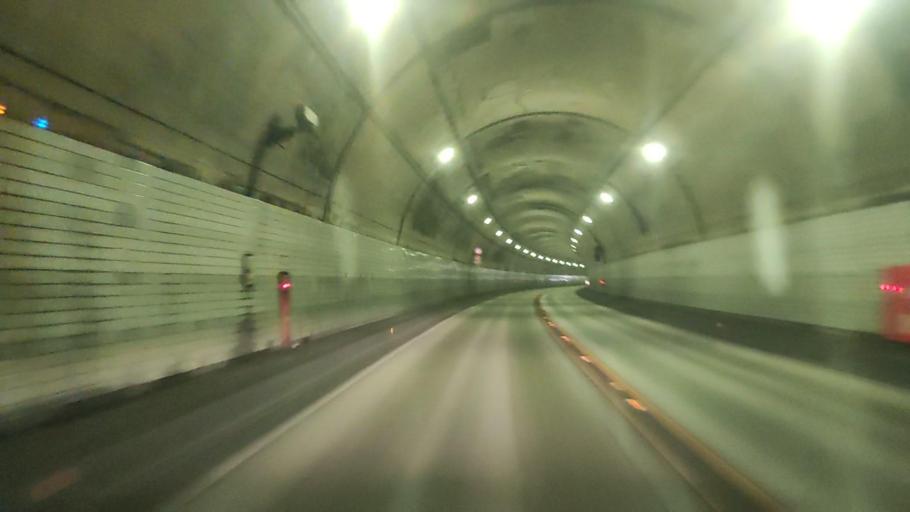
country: JP
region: Fukuoka
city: Maebaru-chuo
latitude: 33.4797
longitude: 130.2889
